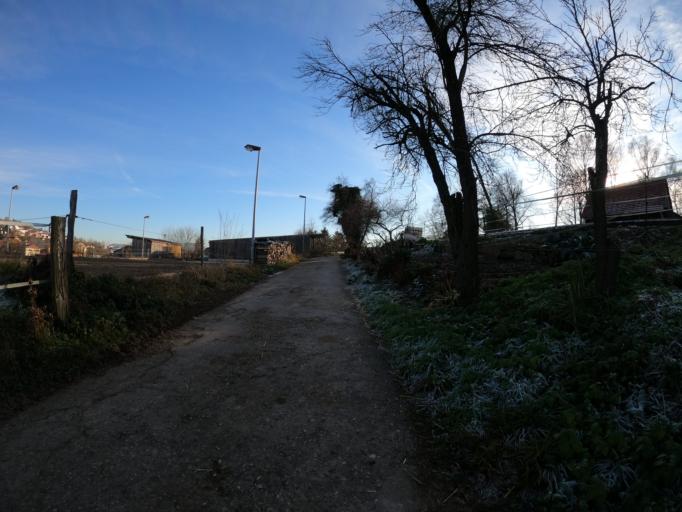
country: DE
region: Baden-Wuerttemberg
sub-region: Regierungsbezirk Stuttgart
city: Goeppingen
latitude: 48.6857
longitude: 9.6257
